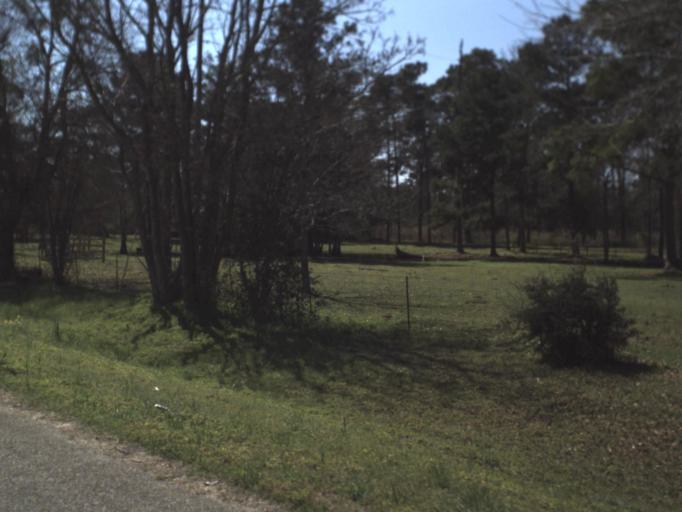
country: US
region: Florida
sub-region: Calhoun County
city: Blountstown
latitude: 30.5679
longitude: -85.0218
